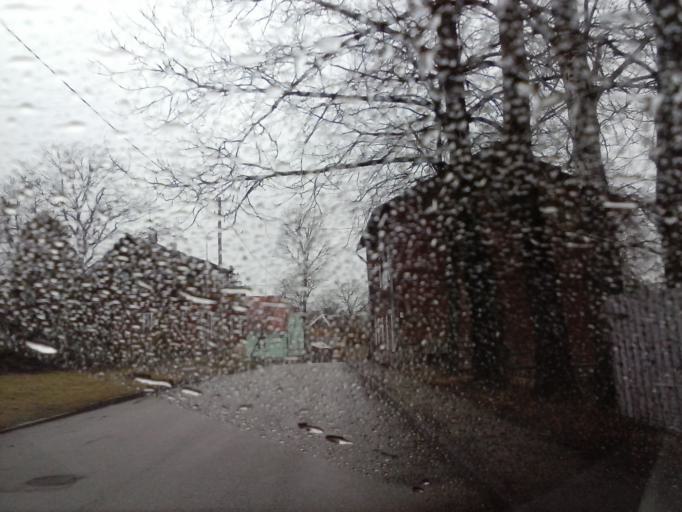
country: EE
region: Valgamaa
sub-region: Valga linn
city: Valga
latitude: 57.7726
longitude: 26.0296
